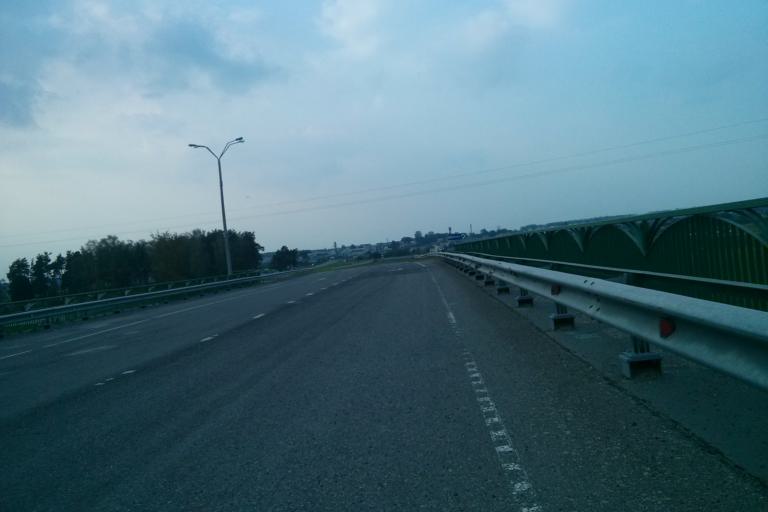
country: BY
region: Minsk
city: Chervyen'
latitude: 53.7240
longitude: 28.3944
